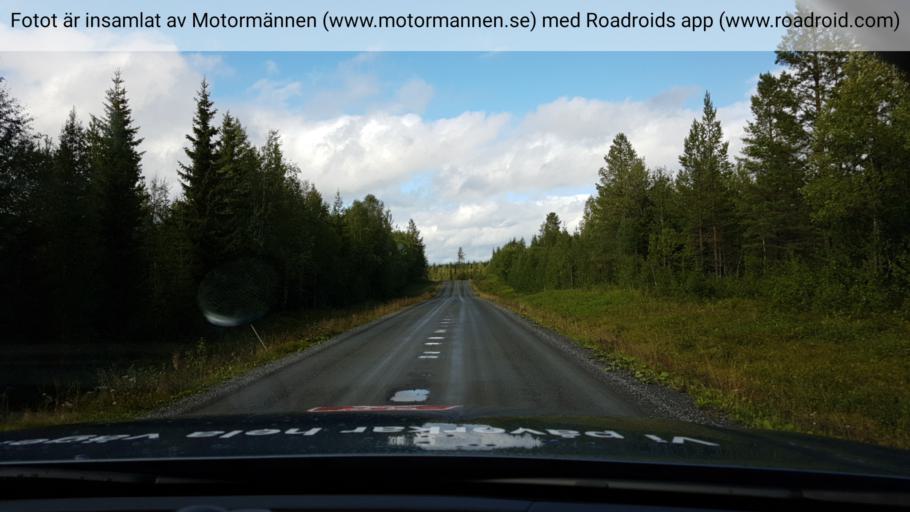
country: SE
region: Jaemtland
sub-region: Krokoms Kommun
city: Krokom
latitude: 63.7200
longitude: 14.5159
